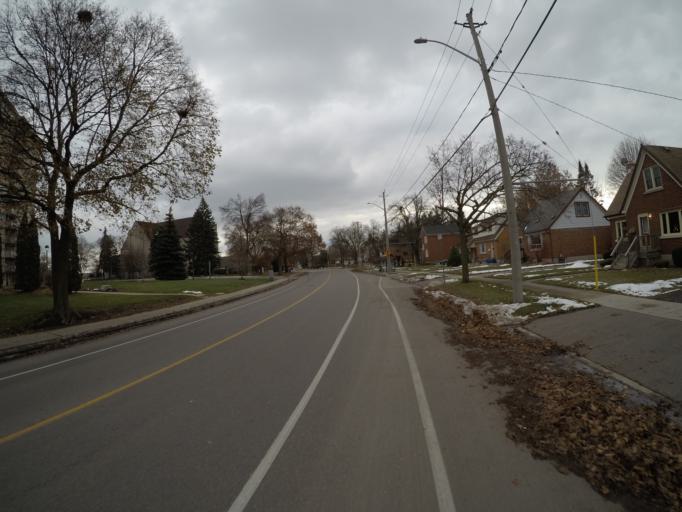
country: CA
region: Ontario
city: Waterloo
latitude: 43.4611
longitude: -80.4931
